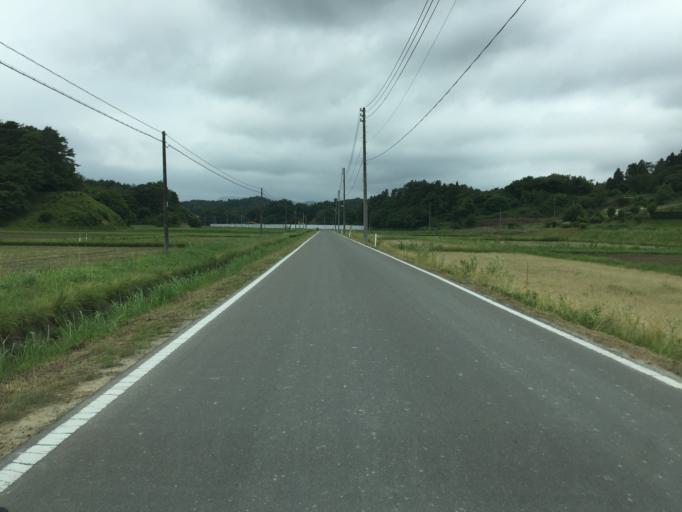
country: JP
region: Fukushima
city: Namie
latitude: 37.7307
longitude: 140.9618
